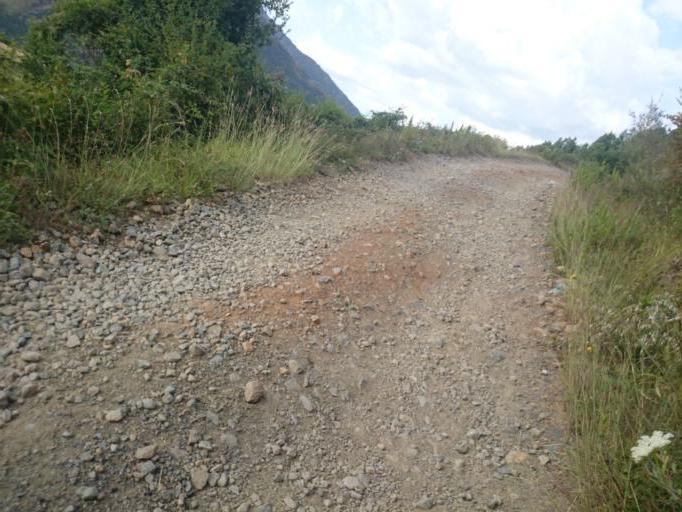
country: AL
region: Elbasan
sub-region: Rrethi i Gramshit
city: Lenias
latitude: 40.7766
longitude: 20.3788
